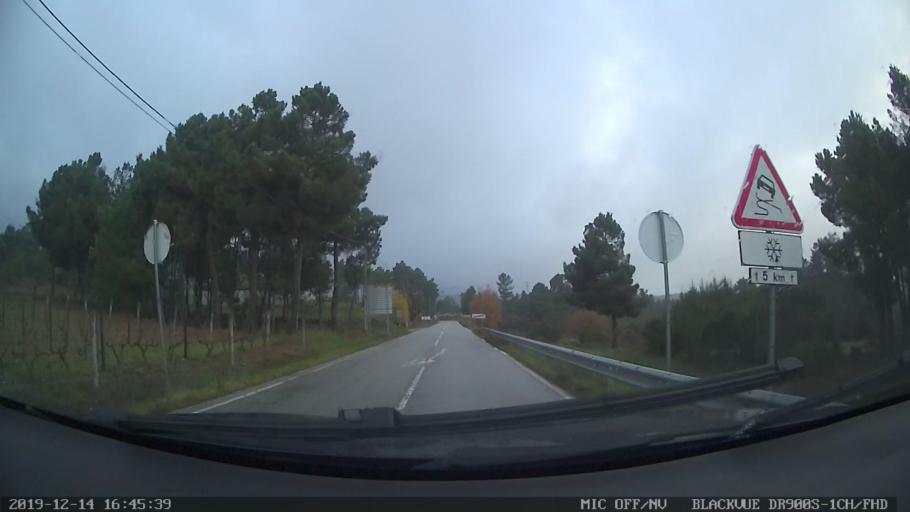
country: PT
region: Vila Real
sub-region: Murca
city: Murca
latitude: 41.4000
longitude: -7.4893
